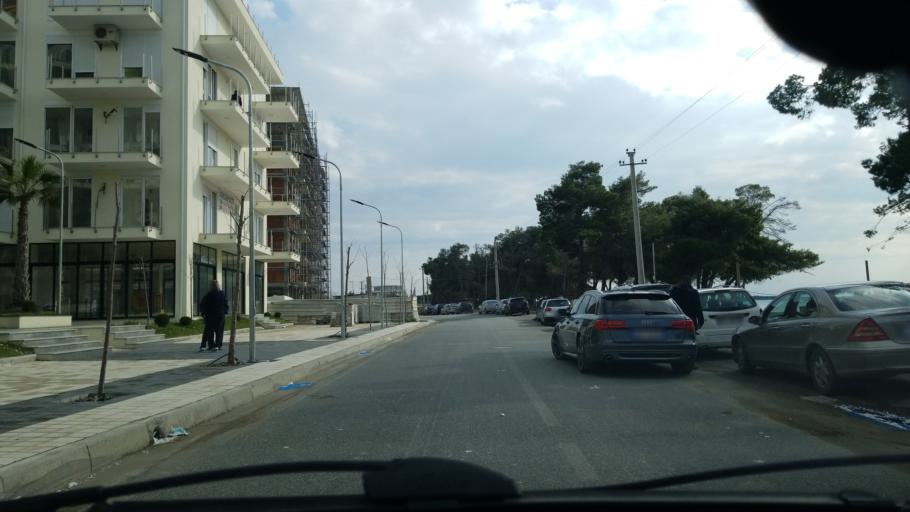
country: AL
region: Lezhe
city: Shengjin
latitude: 41.7933
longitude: 19.6026
